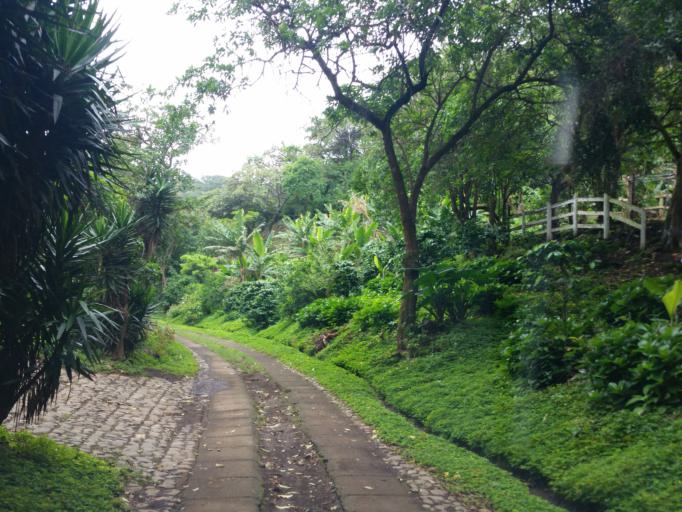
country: NI
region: Managua
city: El Crucero
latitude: 11.9920
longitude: -86.2980
